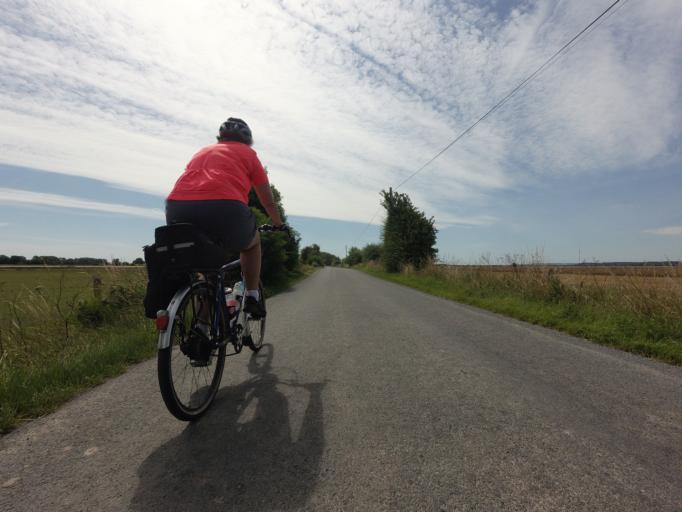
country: GB
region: England
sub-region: Kent
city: Stone
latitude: 50.9999
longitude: 0.8031
